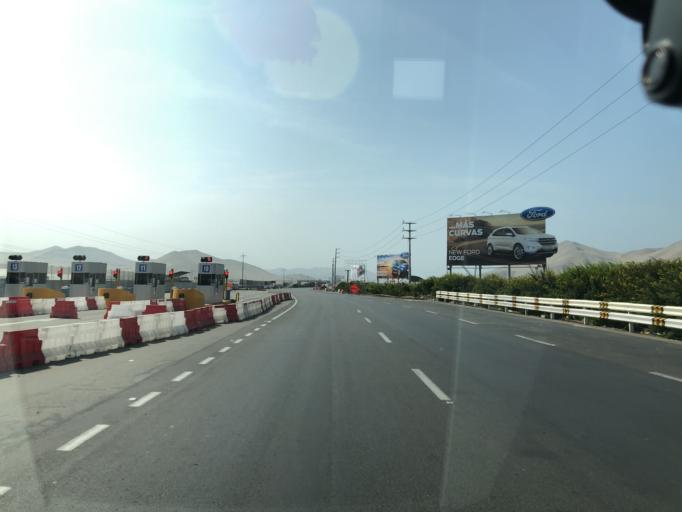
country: PE
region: Lima
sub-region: Provincia de Canete
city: Chilca
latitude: -12.5343
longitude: -76.7208
